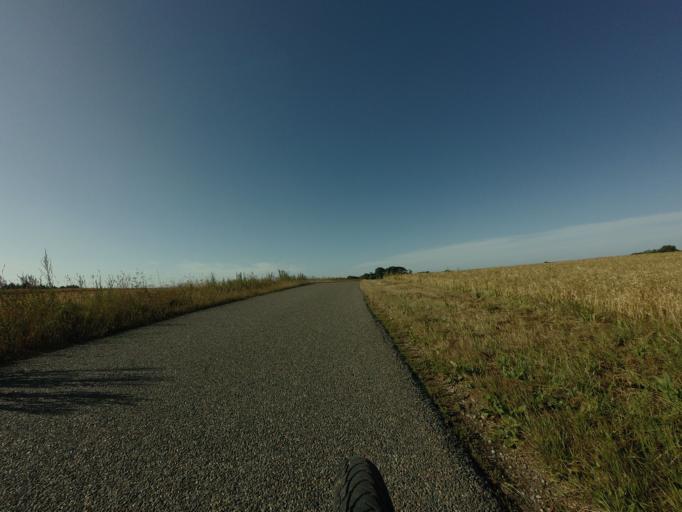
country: DK
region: North Denmark
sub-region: Hjorring Kommune
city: Vra
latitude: 57.3780
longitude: 9.9577
